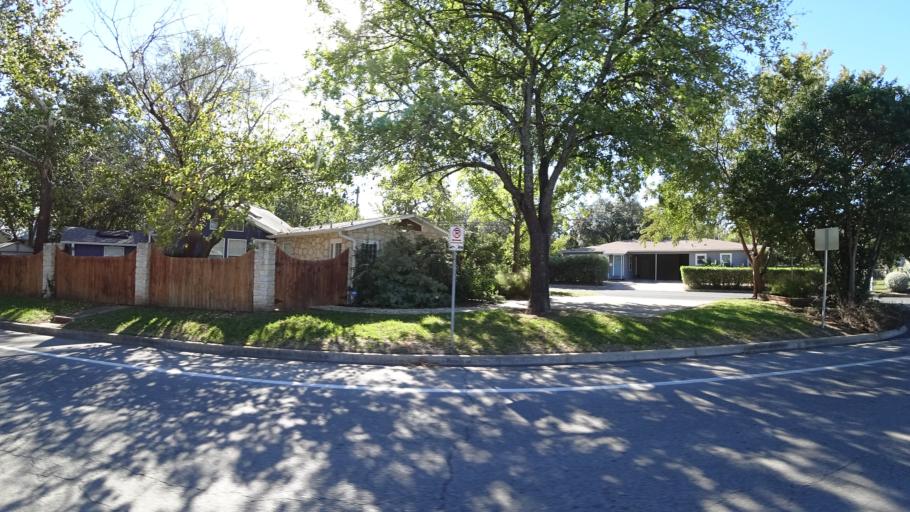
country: US
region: Texas
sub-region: Travis County
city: Austin
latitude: 30.3129
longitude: -97.7529
